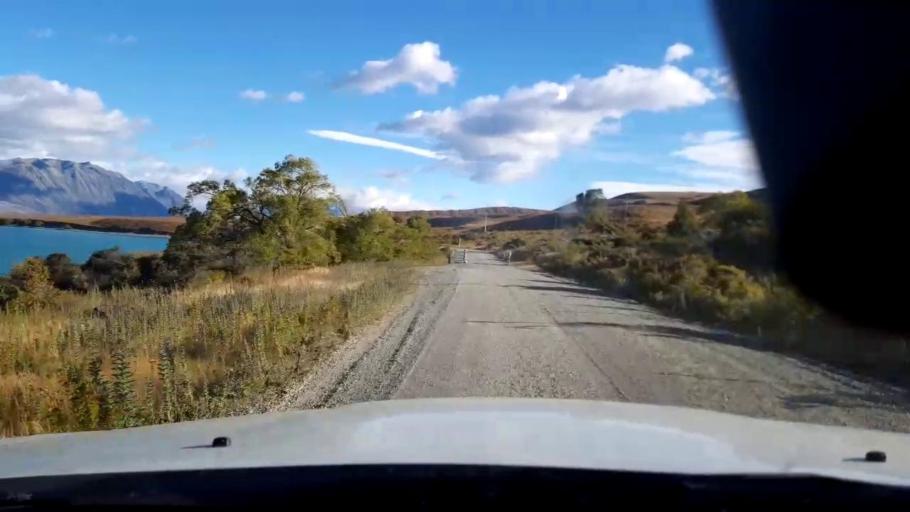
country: NZ
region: Canterbury
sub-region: Timaru District
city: Pleasant Point
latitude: -43.9298
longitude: 170.5600
